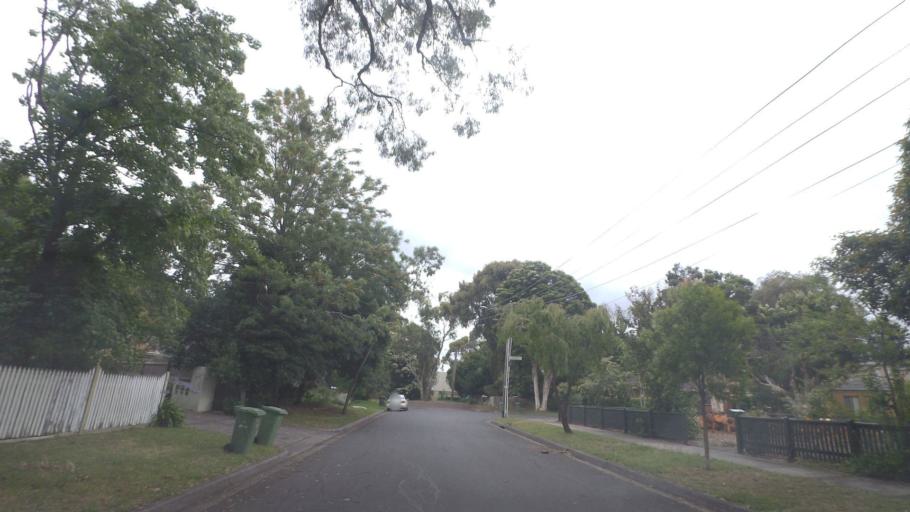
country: AU
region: Victoria
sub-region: Knox
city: Bayswater
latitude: -37.8350
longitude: 145.2774
